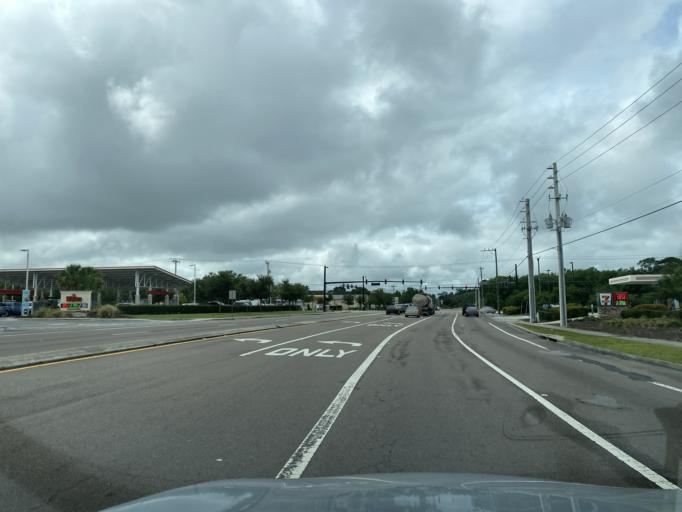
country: US
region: Florida
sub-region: Seminole County
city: Sanford
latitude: 28.7877
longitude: -81.2978
